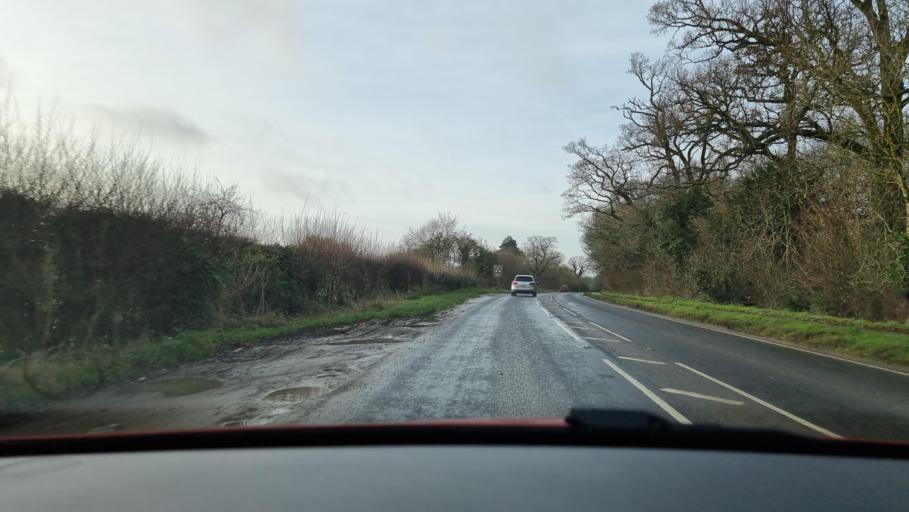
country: GB
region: England
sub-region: Buckinghamshire
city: Winslow
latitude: 51.9504
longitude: -0.8927
